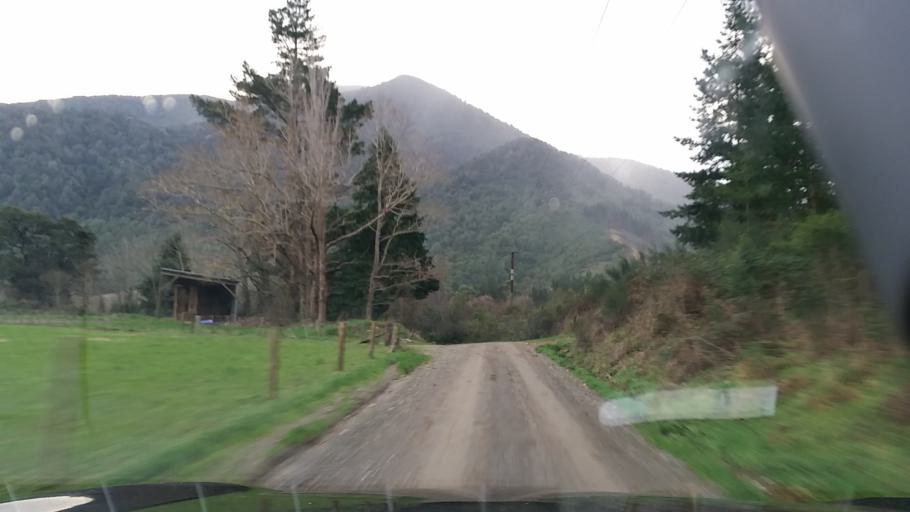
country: NZ
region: Marlborough
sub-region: Marlborough District
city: Picton
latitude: -41.2059
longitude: 173.6898
